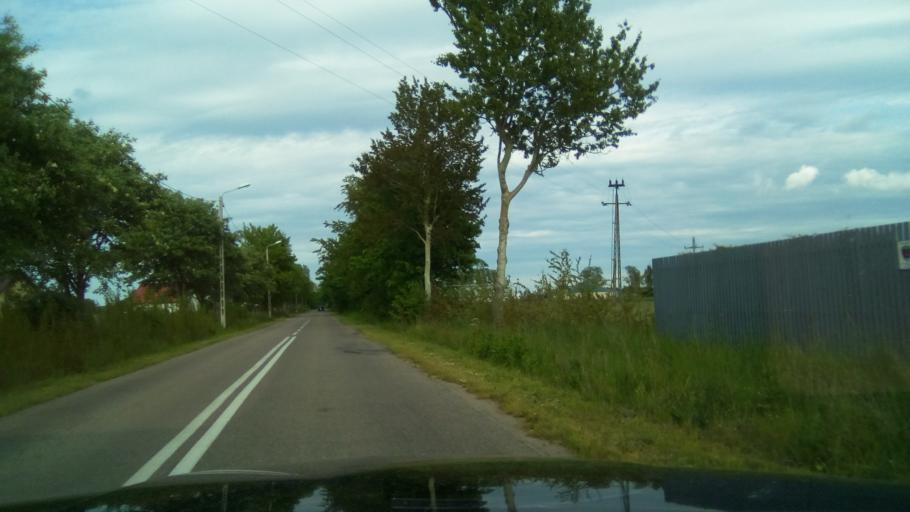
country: PL
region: Pomeranian Voivodeship
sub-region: Powiat pucki
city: Krokowa
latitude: 54.8080
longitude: 18.1797
